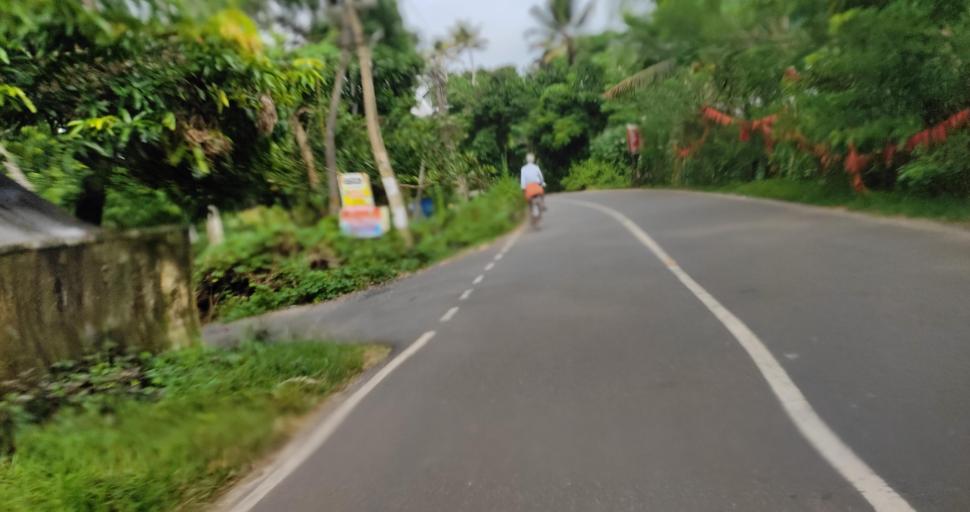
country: IN
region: Kerala
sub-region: Alappuzha
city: Vayalar
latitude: 9.6547
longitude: 76.3090
